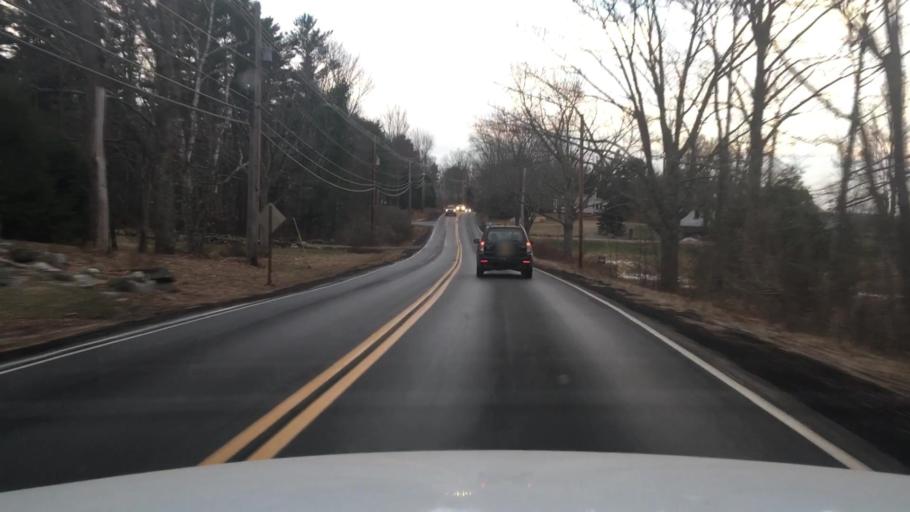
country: US
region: Maine
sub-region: Lincoln County
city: Damariscotta
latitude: 44.0142
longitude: -69.5312
